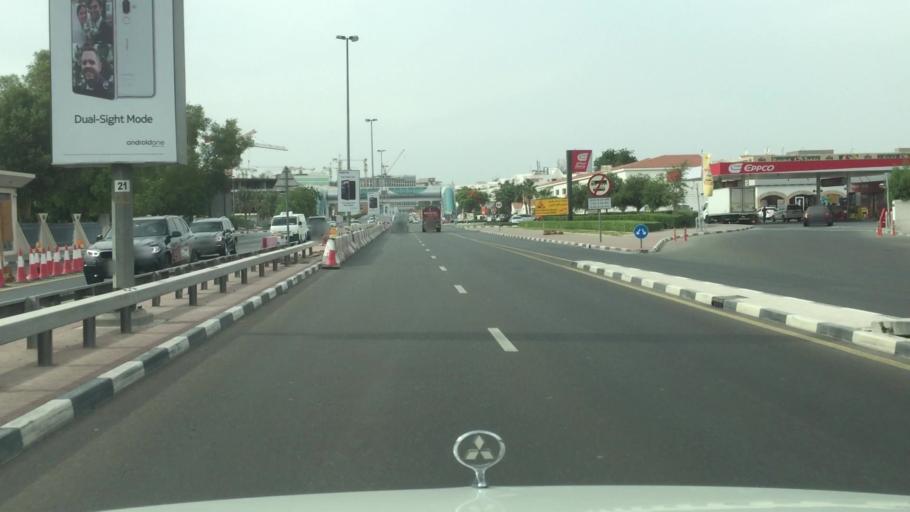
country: AE
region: Ash Shariqah
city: Sharjah
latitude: 25.2413
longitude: 55.3446
